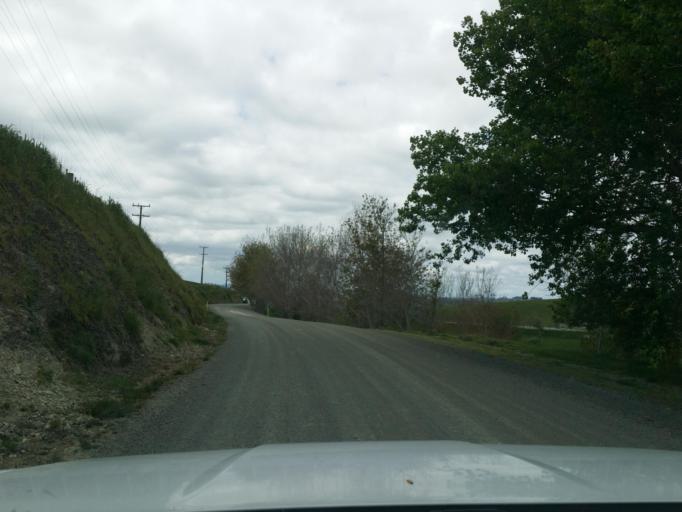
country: NZ
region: Auckland
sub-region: Auckland
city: Wellsford
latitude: -36.2867
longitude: 174.3480
